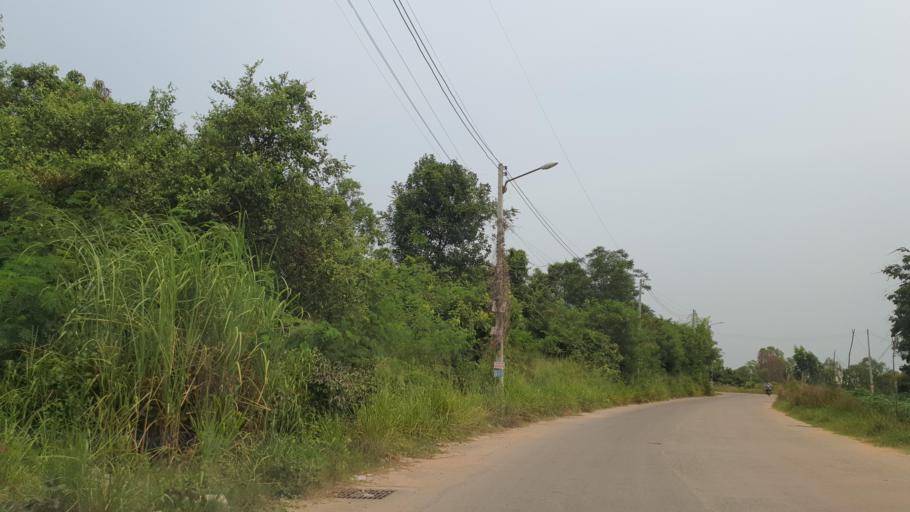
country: TH
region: Chon Buri
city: Phatthaya
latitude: 12.8846
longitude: 100.9267
